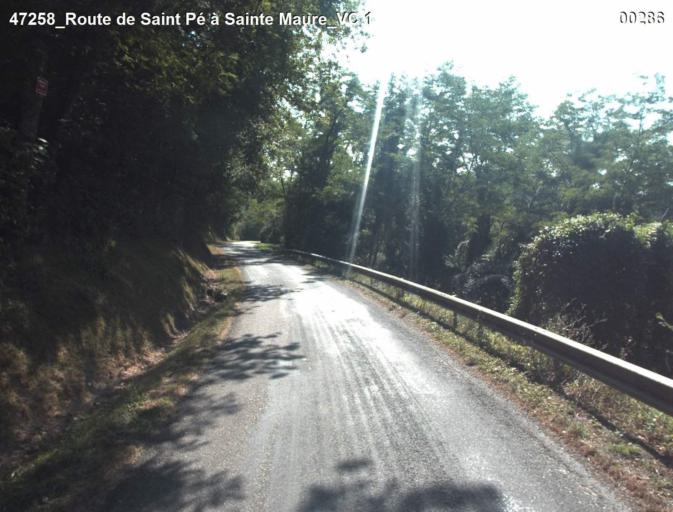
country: FR
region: Midi-Pyrenees
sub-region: Departement du Gers
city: Montreal
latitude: 44.0170
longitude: 0.1263
